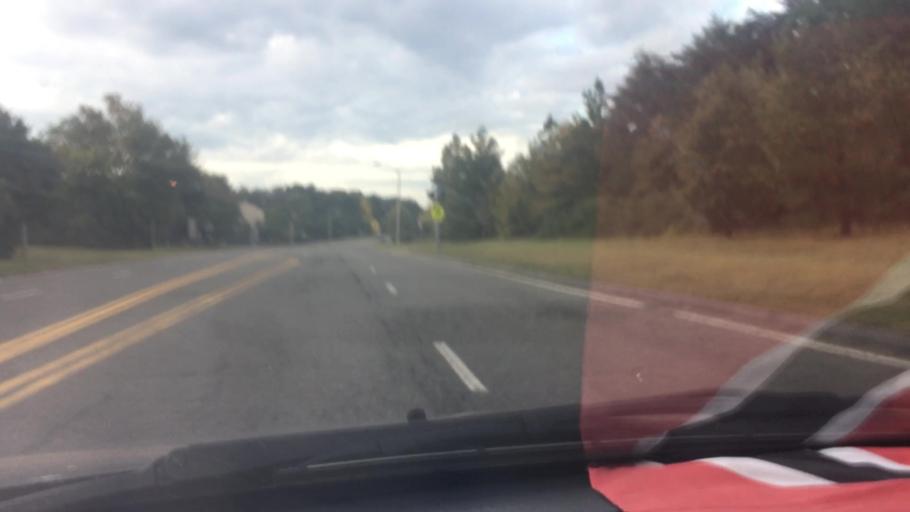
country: US
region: Maryland
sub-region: Prince George's County
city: District Heights
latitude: 38.8461
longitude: -76.9046
